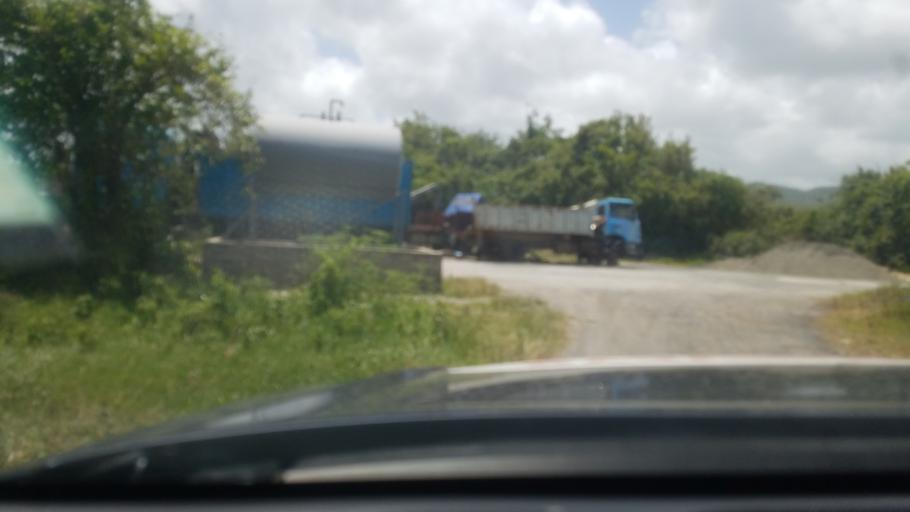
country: LC
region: Vieux-Fort
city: Vieux Fort
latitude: 13.7448
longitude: -60.9456
